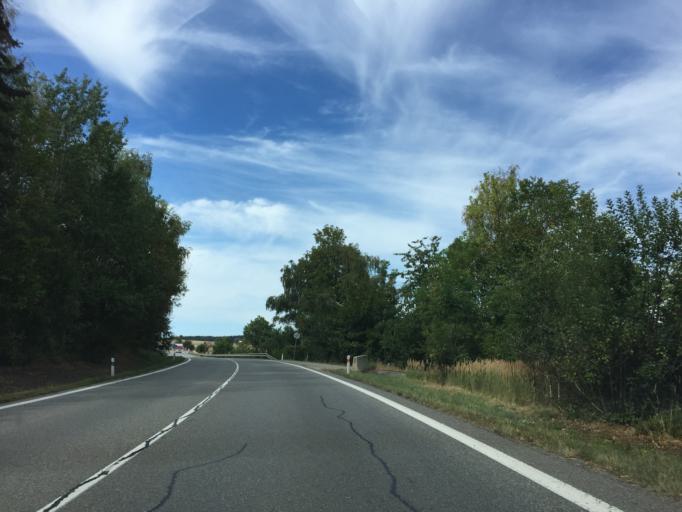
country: CZ
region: Jihocesky
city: Chotoviny
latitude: 49.5551
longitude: 14.6662
